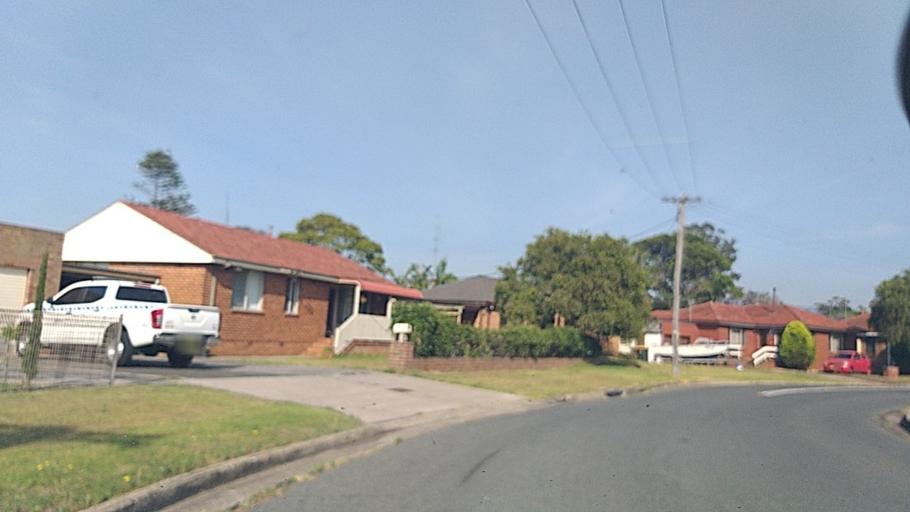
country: AU
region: New South Wales
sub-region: Wollongong
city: Berkeley
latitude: -34.4813
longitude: 150.8499
